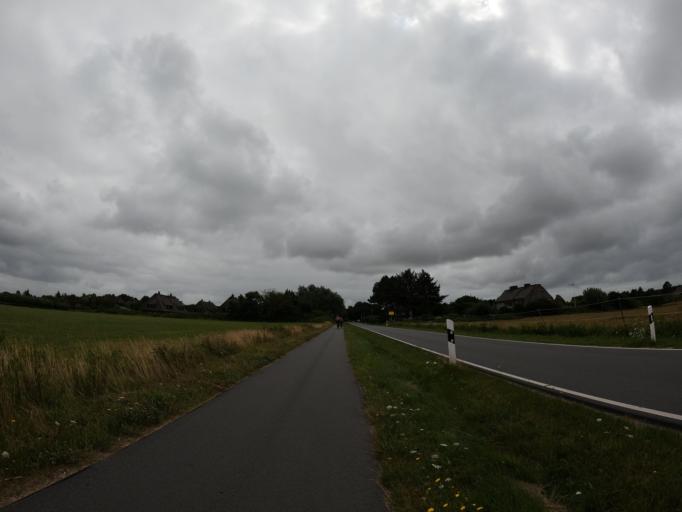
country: DE
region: Schleswig-Holstein
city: Tinnum
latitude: 54.9344
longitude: 8.3497
